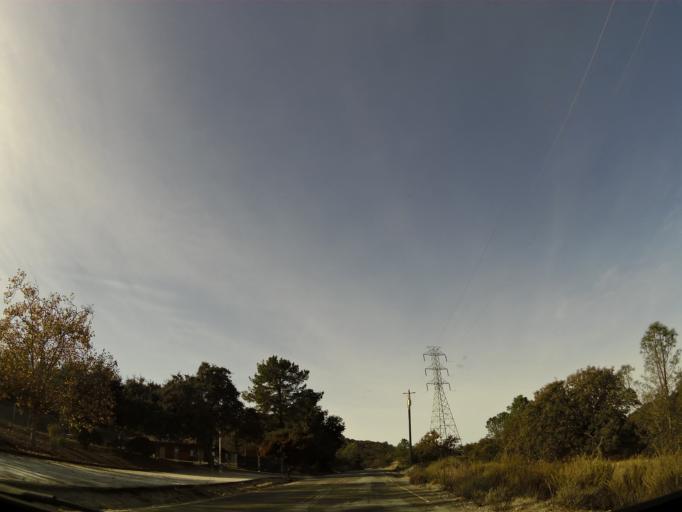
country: US
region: California
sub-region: San Benito County
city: Ridgemark
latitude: 36.7299
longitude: -121.3605
